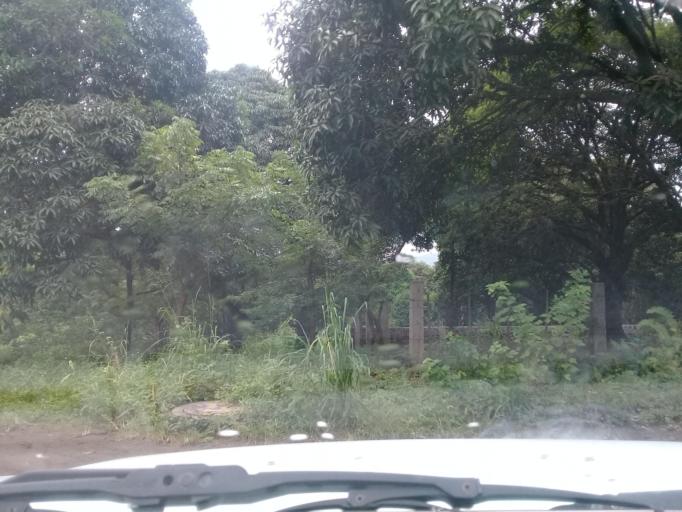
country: MX
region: Veracruz
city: San Andres Tuxtla
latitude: 18.4378
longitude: -95.2070
